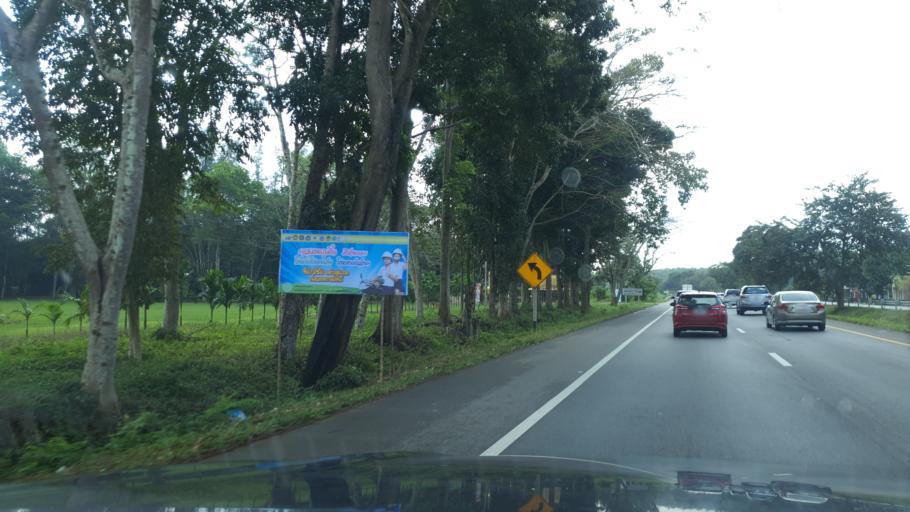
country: TH
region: Chumphon
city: Tha Sae
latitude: 10.7838
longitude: 99.1901
